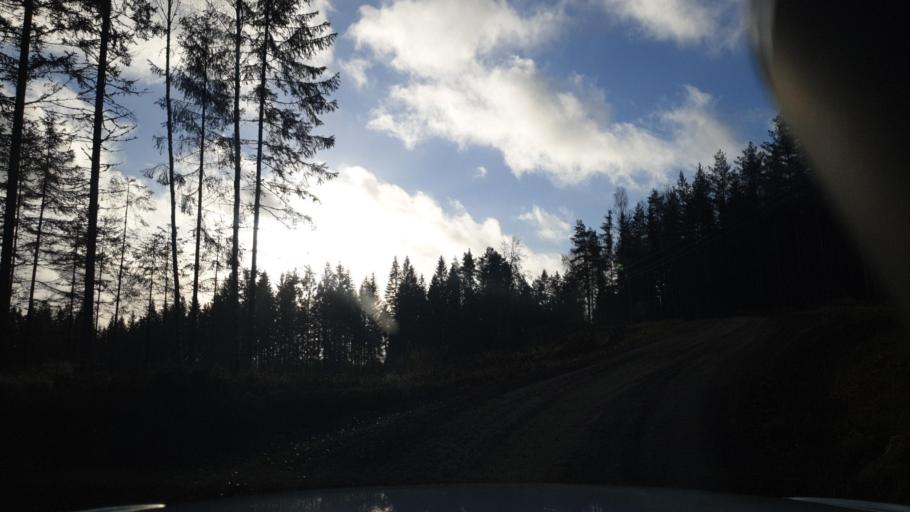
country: SE
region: Vaermland
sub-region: Grums Kommun
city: Grums
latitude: 59.4972
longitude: 12.9260
